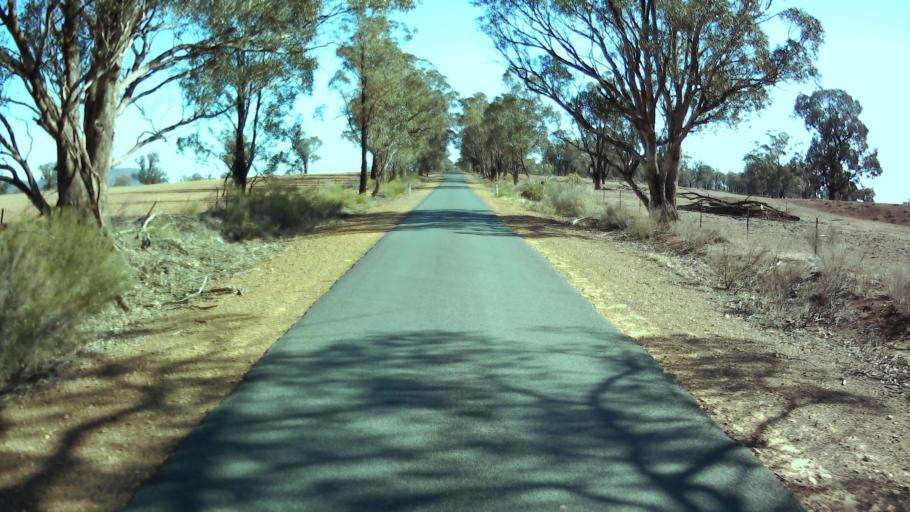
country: AU
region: New South Wales
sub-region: Weddin
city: Grenfell
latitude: -33.7898
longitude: 147.9577
